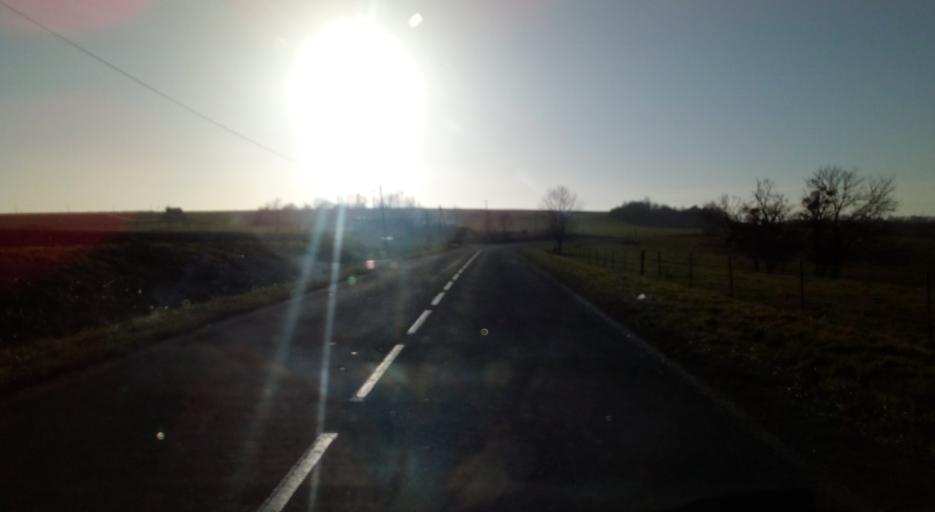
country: FR
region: Champagne-Ardenne
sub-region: Departement des Ardennes
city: Signy-le-Petit
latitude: 49.7620
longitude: 4.3337
